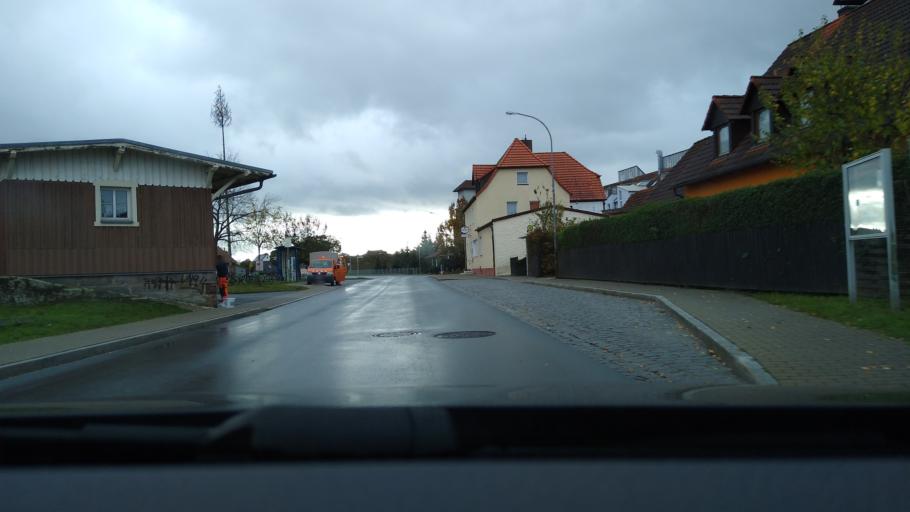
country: DE
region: Bavaria
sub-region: Regierungsbezirk Mittelfranken
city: Hemhofen
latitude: 49.6917
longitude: 10.9386
